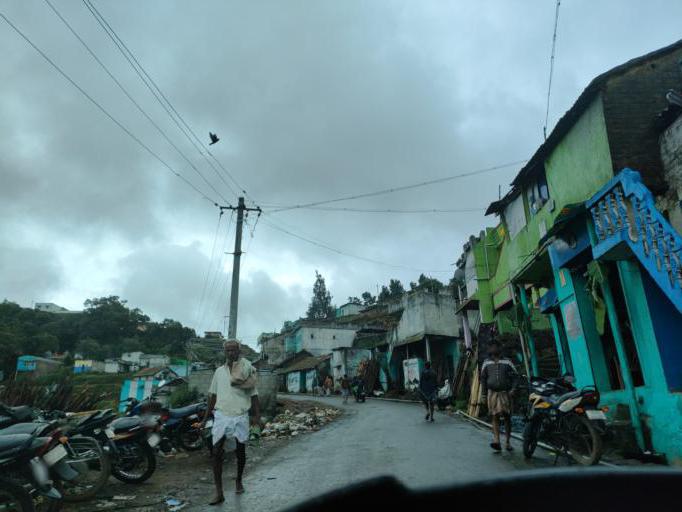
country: IN
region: Tamil Nadu
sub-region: Dindigul
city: Kodaikanal
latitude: 10.2237
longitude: 77.3430
